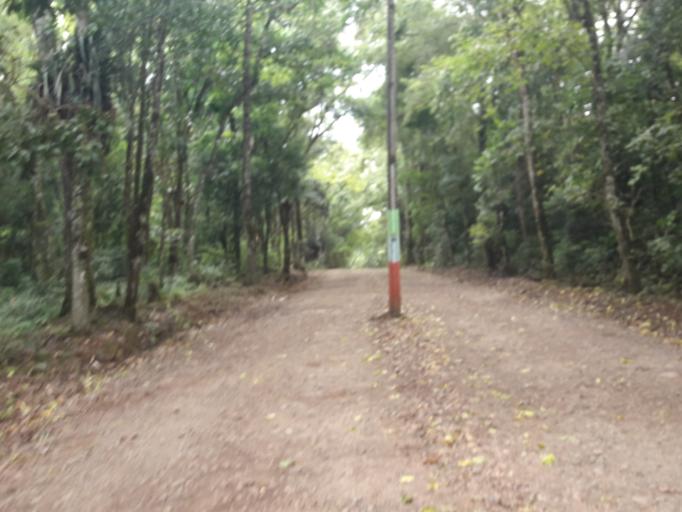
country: BR
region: Rio Grande do Sul
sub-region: Frederico Westphalen
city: Frederico Westphalen
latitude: -27.0895
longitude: -53.3800
